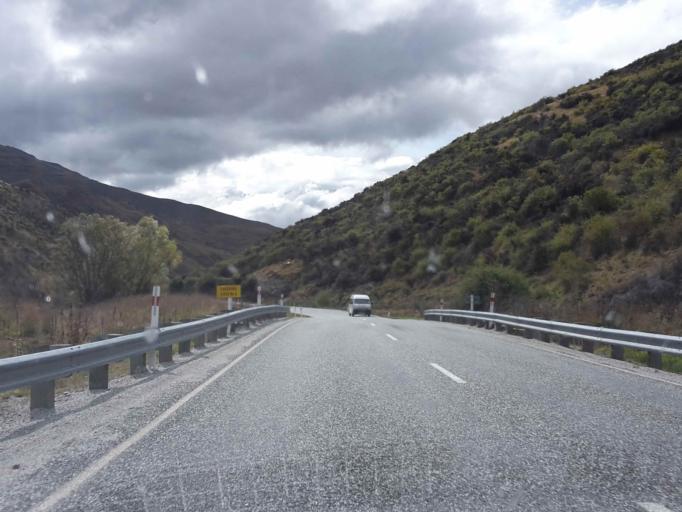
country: NZ
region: Otago
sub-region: Queenstown-Lakes District
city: Arrowtown
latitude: -44.9274
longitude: 168.9715
